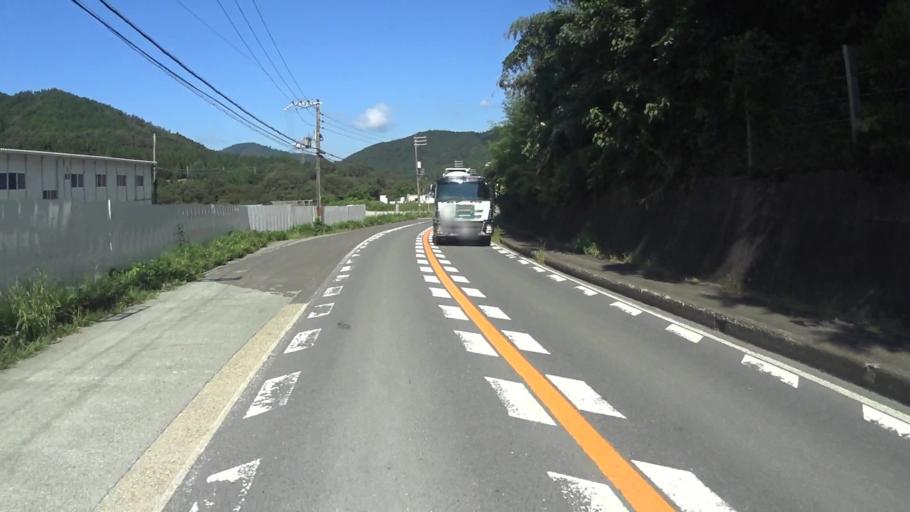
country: JP
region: Kyoto
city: Ayabe
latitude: 35.2905
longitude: 135.3324
